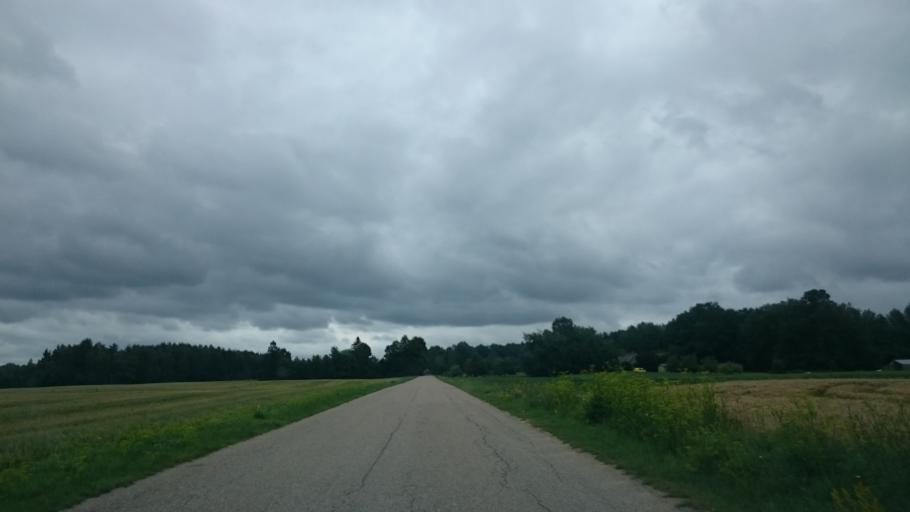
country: LV
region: Aizpute
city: Aizpute
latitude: 56.7145
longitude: 21.4681
